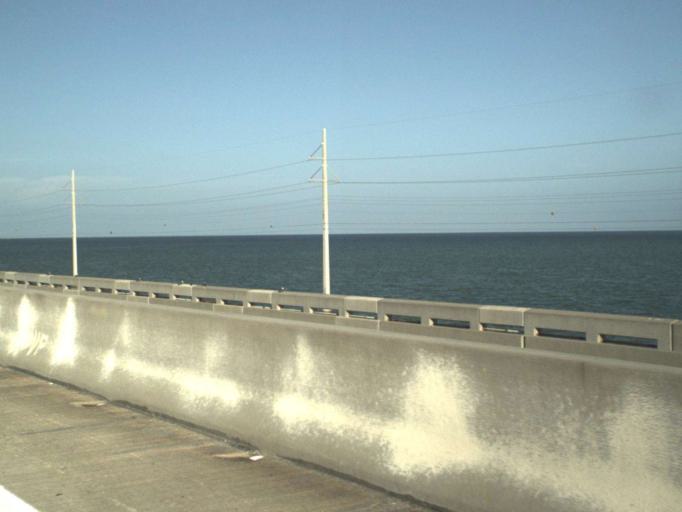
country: US
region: Florida
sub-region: Monroe County
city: Marathon
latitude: 24.8004
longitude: -80.8585
